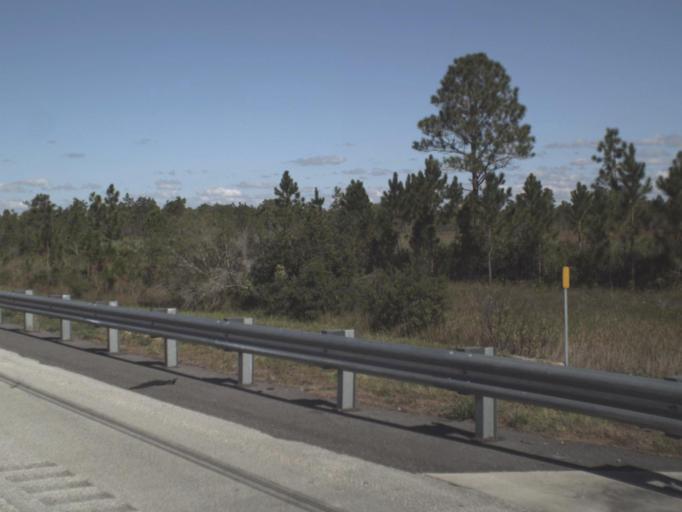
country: US
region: Florida
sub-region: Osceola County
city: Saint Cloud
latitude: 27.9938
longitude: -81.1314
